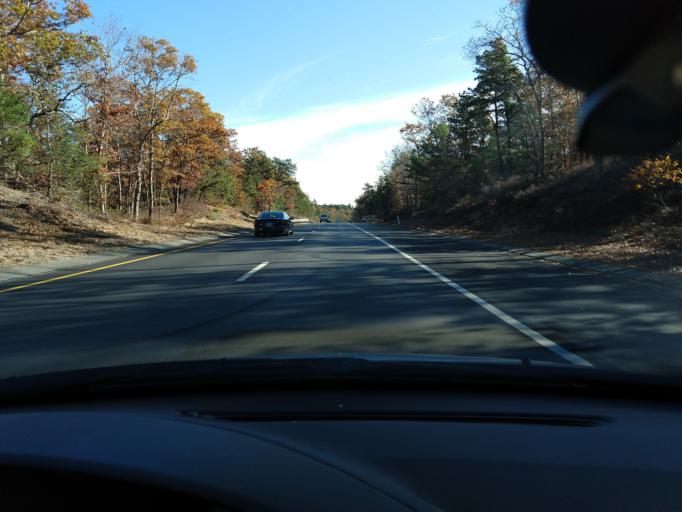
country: US
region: Massachusetts
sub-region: Plymouth County
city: Plymouth
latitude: 41.9290
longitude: -70.6380
